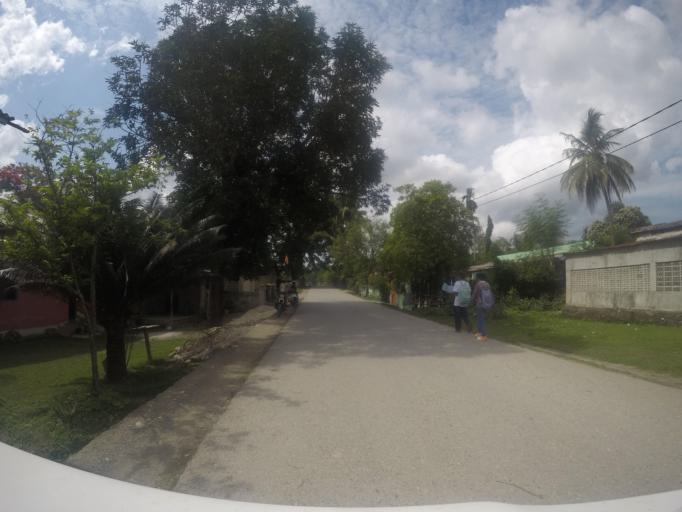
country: TL
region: Viqueque
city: Viqueque
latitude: -8.8578
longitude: 126.3632
